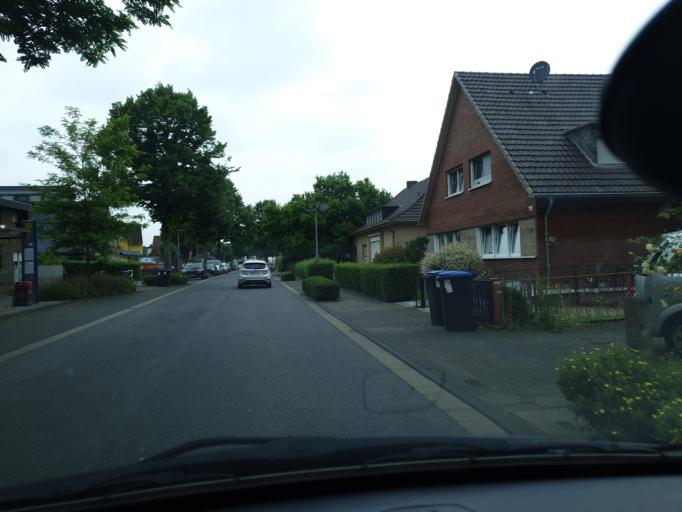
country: DE
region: North Rhine-Westphalia
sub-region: Regierungsbezirk Koln
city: Hurth
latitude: 50.8875
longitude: 6.8444
